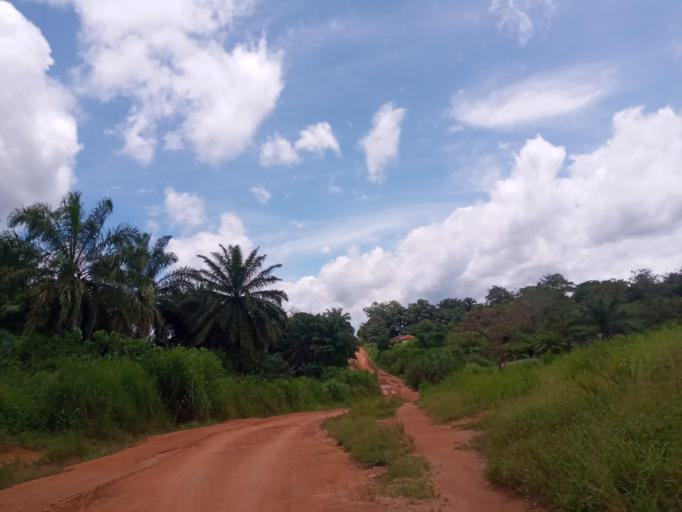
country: SL
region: Eastern Province
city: Koidu
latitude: 8.6449
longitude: -10.9198
